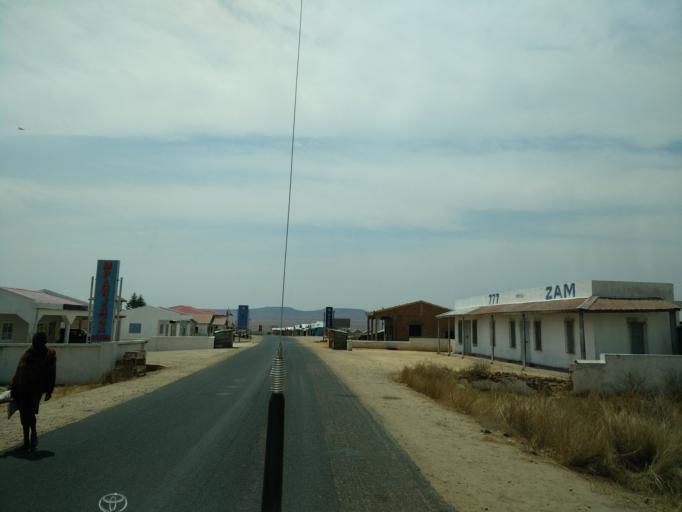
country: MG
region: Ihorombe
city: Ranohira
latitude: -22.7793
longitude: 45.0775
